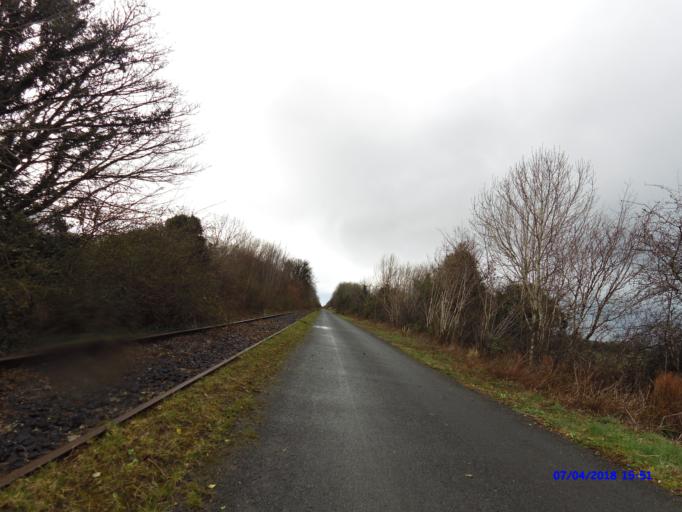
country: IE
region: Leinster
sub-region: An Iarmhi
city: Athlone
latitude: 53.4145
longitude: -7.8556
